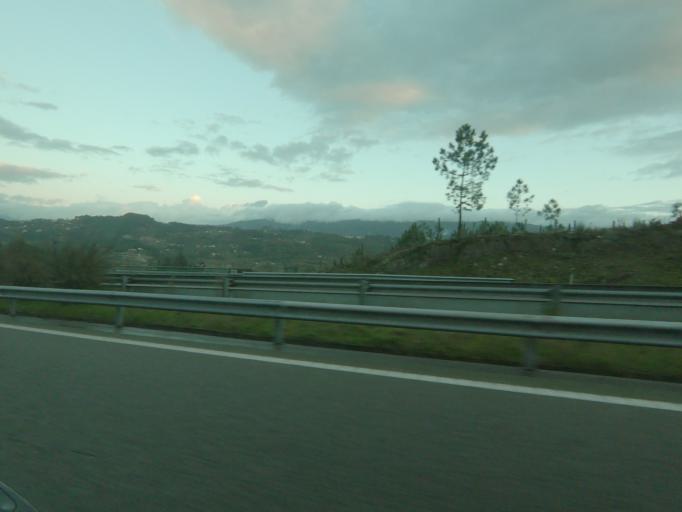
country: PT
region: Porto
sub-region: Marco de Canaveses
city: Marco de Canavezes
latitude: 41.2317
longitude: -8.1273
